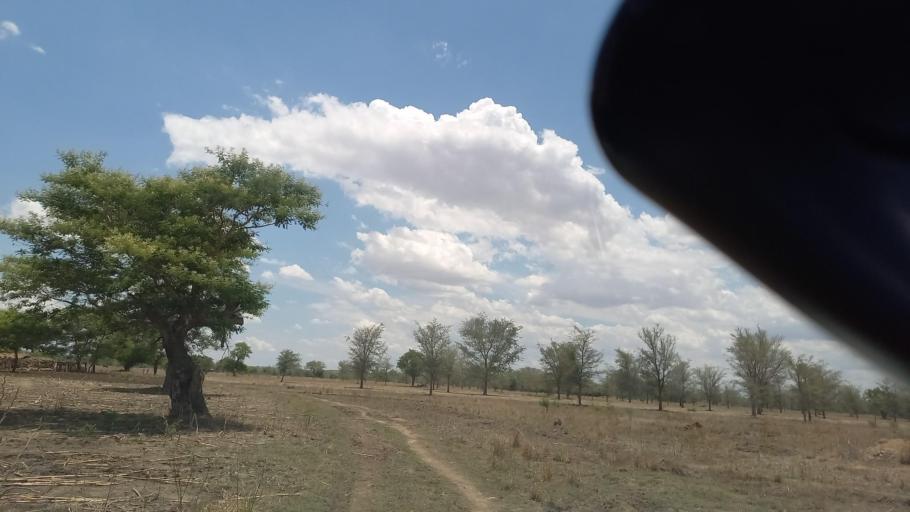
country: ZM
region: Southern
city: Mazabuka
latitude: -16.1248
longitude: 27.7786
